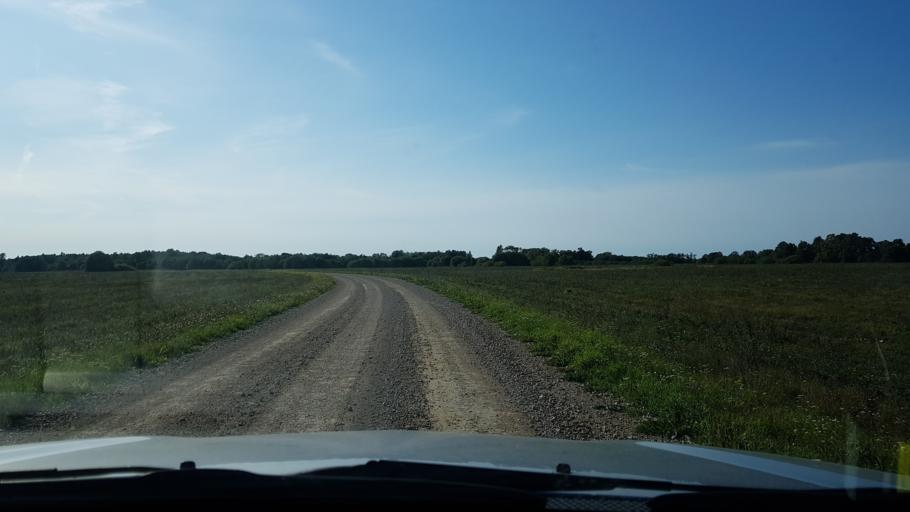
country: EE
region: Ida-Virumaa
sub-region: Narva-Joesuu linn
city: Narva-Joesuu
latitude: 59.4079
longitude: 28.0023
